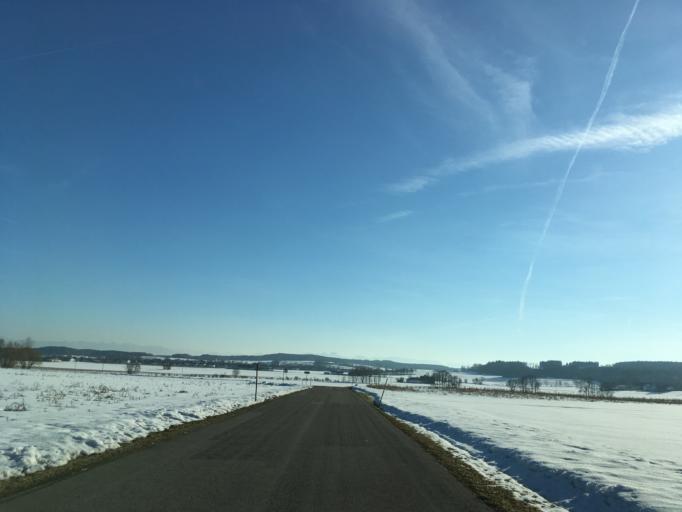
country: DE
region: Bavaria
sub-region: Upper Bavaria
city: Steinhoring
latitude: 48.1053
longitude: 12.0258
